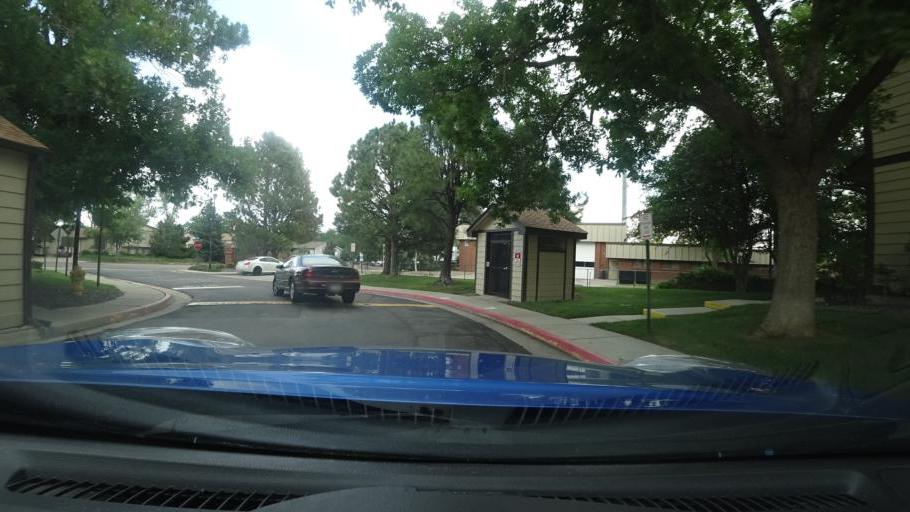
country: US
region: Colorado
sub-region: Adams County
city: Aurora
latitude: 39.6851
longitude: -104.7865
